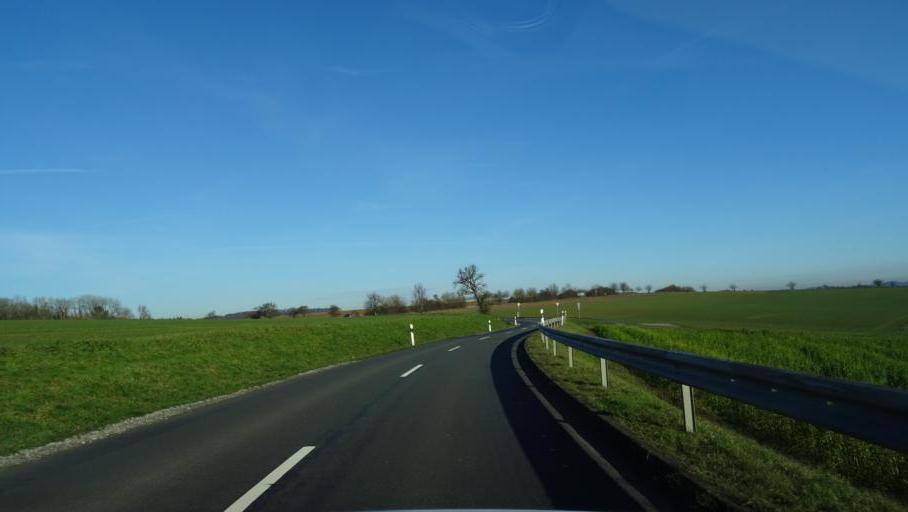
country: DE
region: Baden-Wuerttemberg
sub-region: Karlsruhe Region
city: Obrigheim
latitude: 49.3651
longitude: 9.1126
